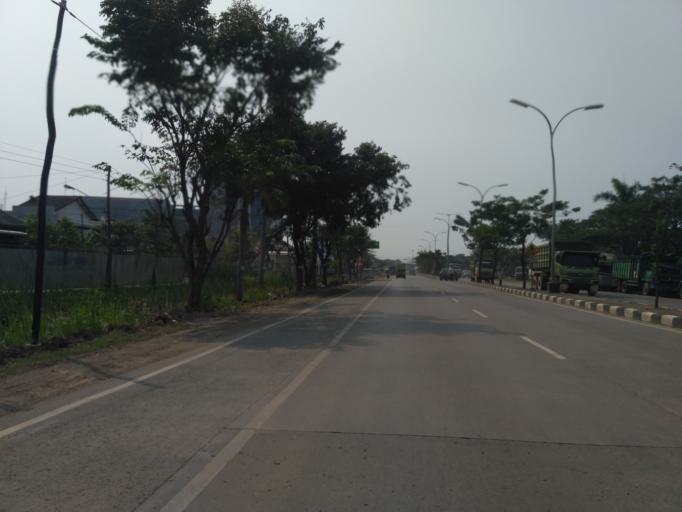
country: ID
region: Central Java
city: Semarang
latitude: -6.9648
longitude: 110.3938
